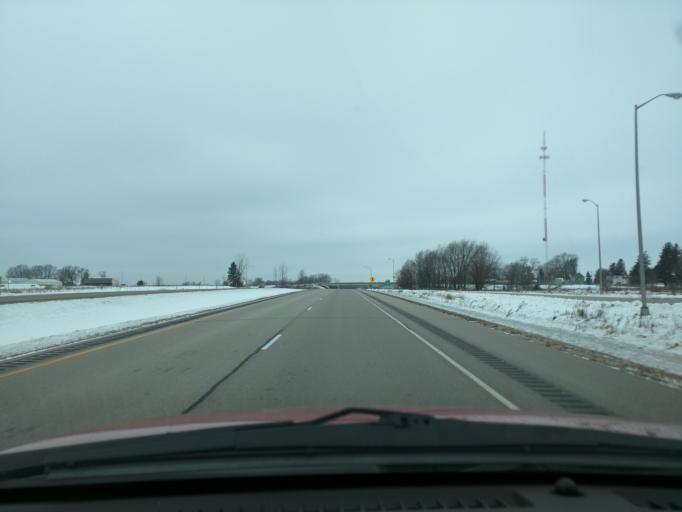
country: US
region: Wisconsin
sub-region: Trempealeau County
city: Trempealeau
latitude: 43.9110
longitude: -91.5543
